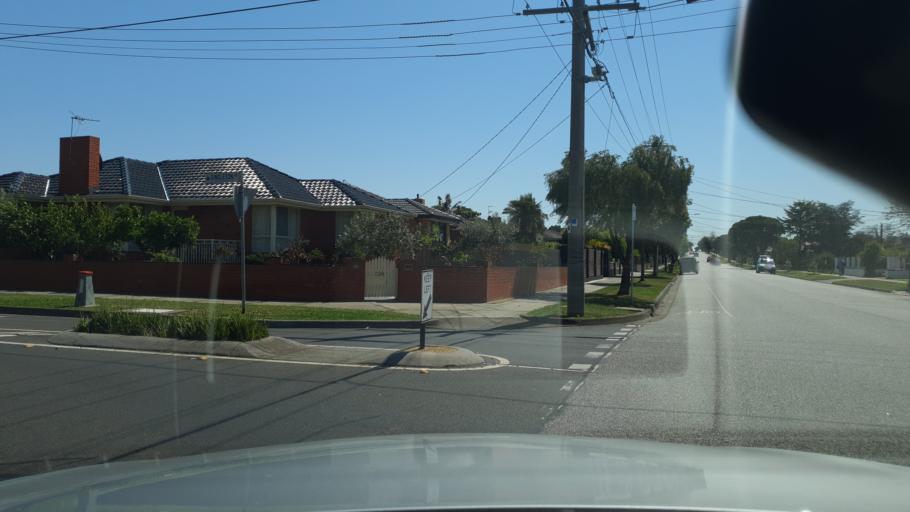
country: AU
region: Victoria
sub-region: Greater Dandenong
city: Springvale
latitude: -37.9342
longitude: 145.1718
